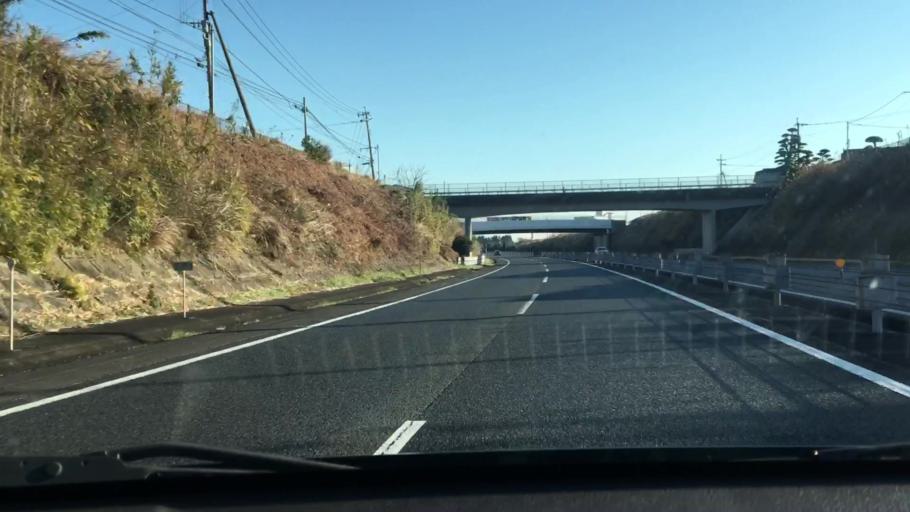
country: JP
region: Kagoshima
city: Kajiki
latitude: 31.8060
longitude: 130.7089
